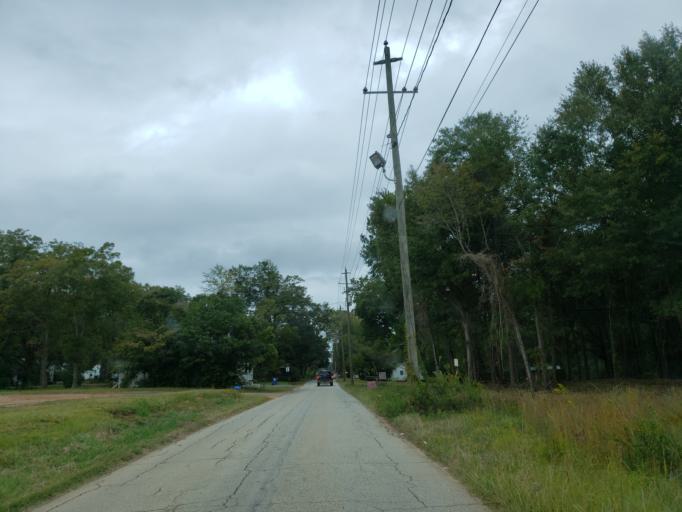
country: US
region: Georgia
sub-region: Monroe County
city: Forsyth
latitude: 33.0318
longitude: -83.9273
